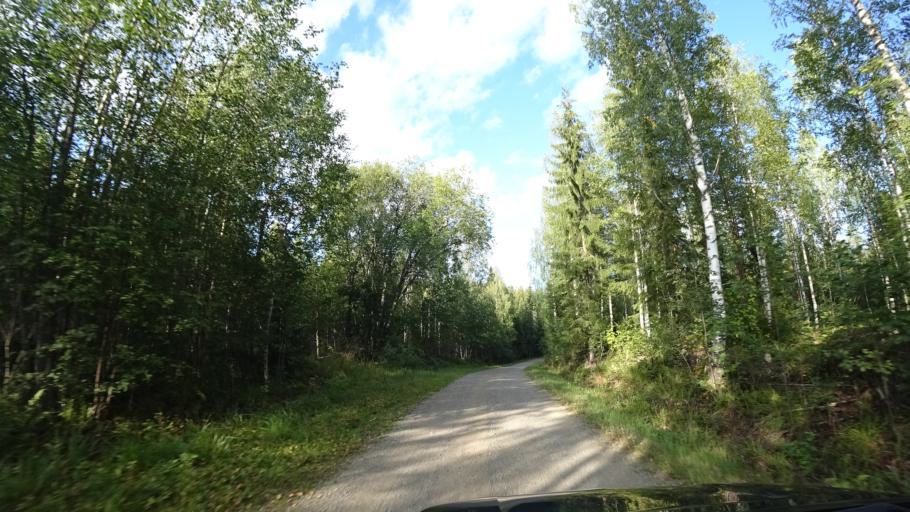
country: FI
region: Paijanne Tavastia
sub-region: Lahti
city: Auttoinen
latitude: 61.2144
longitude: 25.1720
